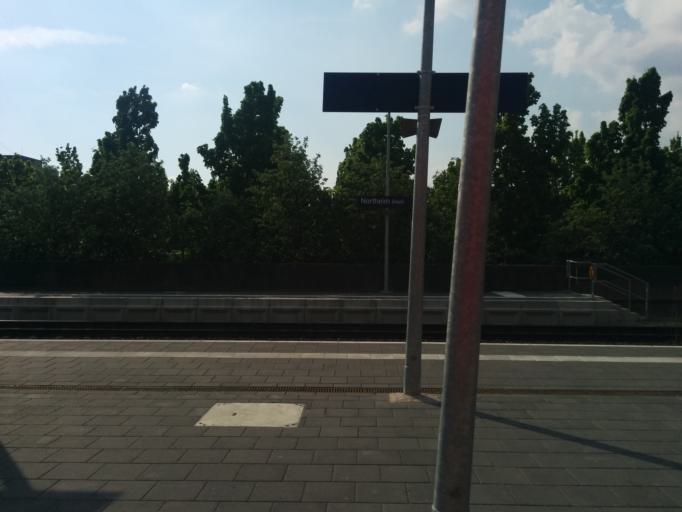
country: DE
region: Lower Saxony
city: Northeim
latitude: 51.7040
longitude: 9.9876
